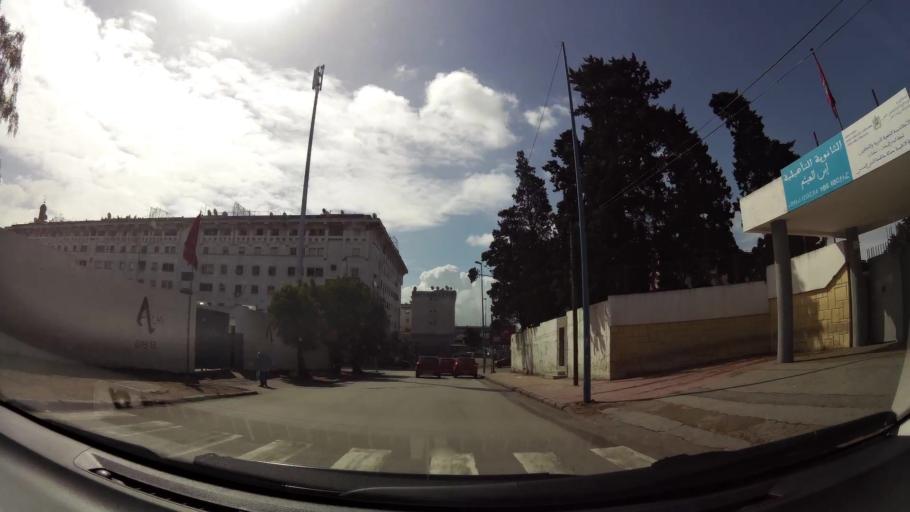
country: MA
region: Grand Casablanca
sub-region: Casablanca
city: Casablanca
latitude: 33.5683
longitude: -7.6774
